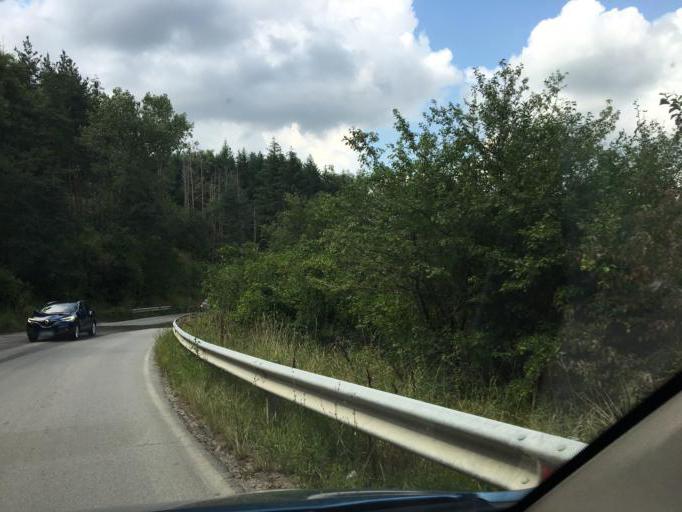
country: BG
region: Sofia-Capital
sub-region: Stolichna Obshtina
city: Sofia
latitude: 42.5942
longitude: 23.3651
